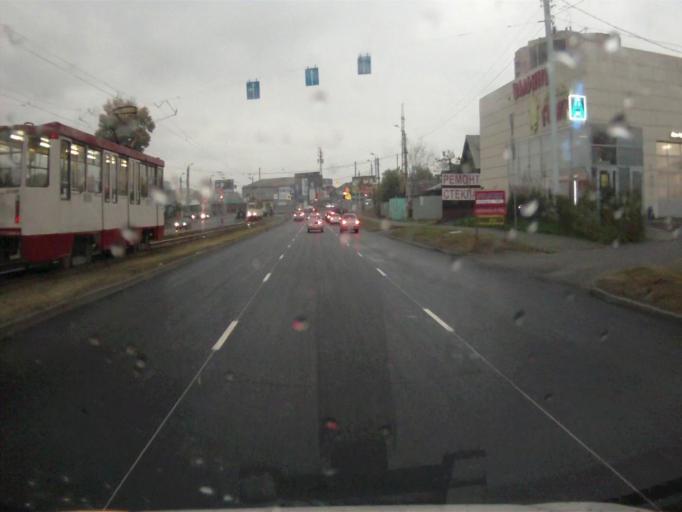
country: RU
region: Chelyabinsk
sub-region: Gorod Chelyabinsk
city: Chelyabinsk
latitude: 55.1838
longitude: 61.3747
